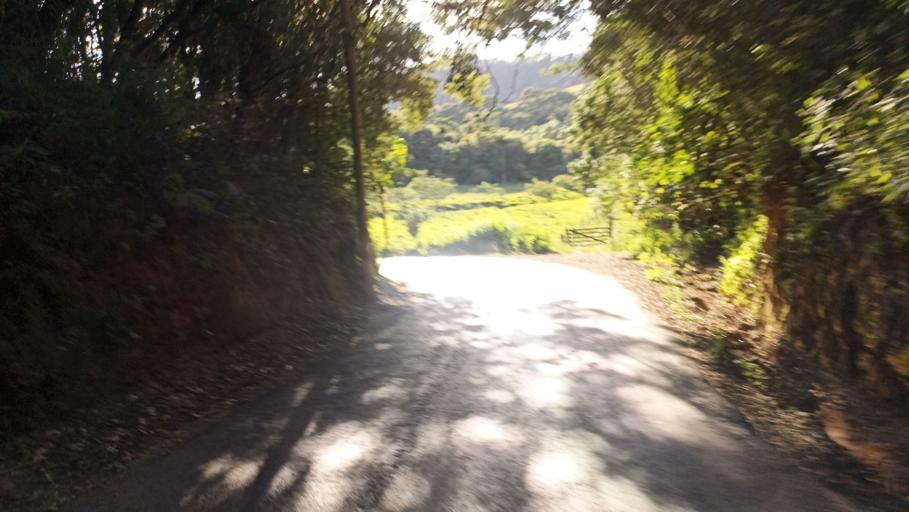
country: BR
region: Minas Gerais
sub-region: Ouro Preto
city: Ouro Preto
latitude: -20.3086
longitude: -43.6026
